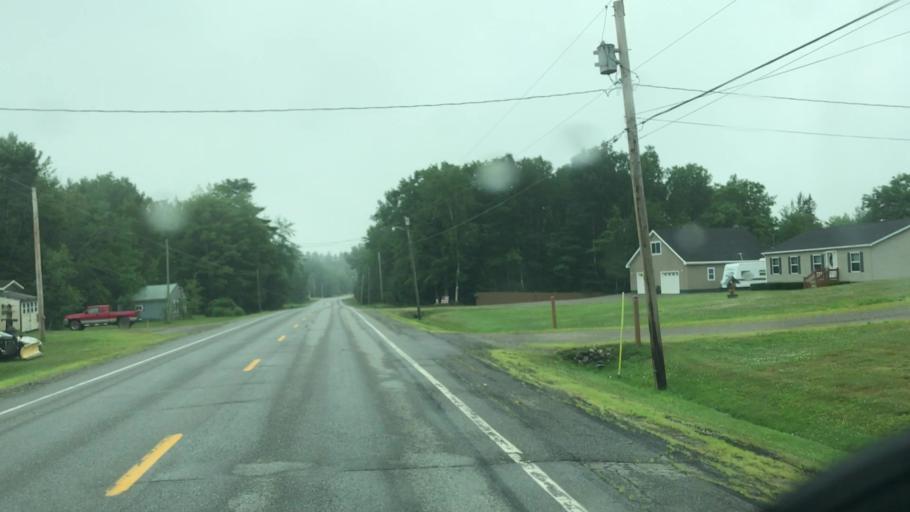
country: US
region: Maine
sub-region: Penobscot County
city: Howland
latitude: 45.2581
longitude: -68.6379
